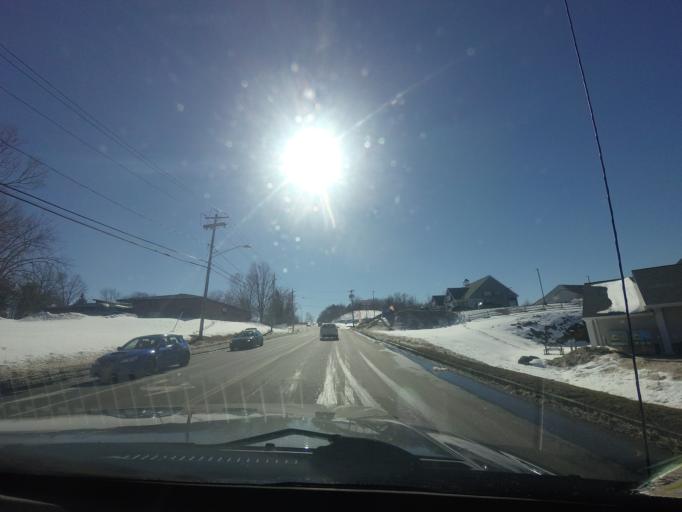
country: US
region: New York
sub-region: Saratoga County
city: Waterford
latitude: 42.7841
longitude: -73.6546
